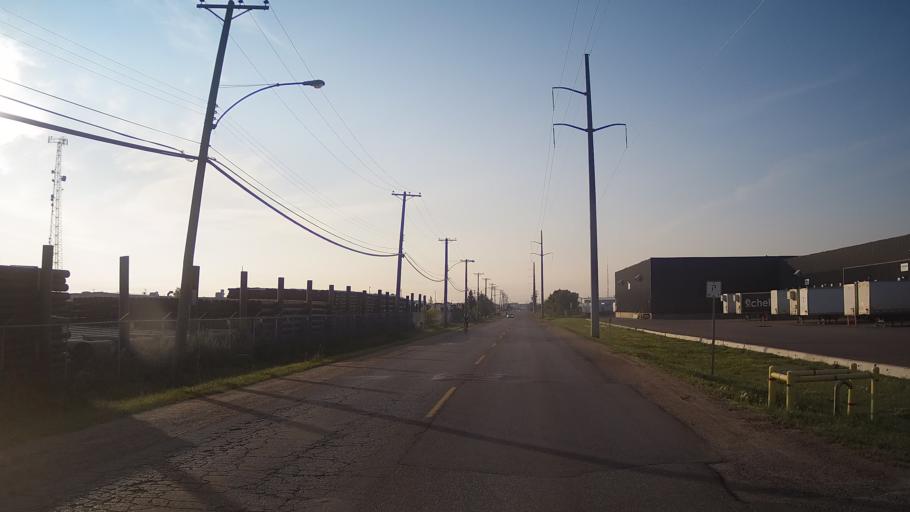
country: CA
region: Saskatchewan
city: Saskatoon
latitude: 52.0875
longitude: -106.6629
